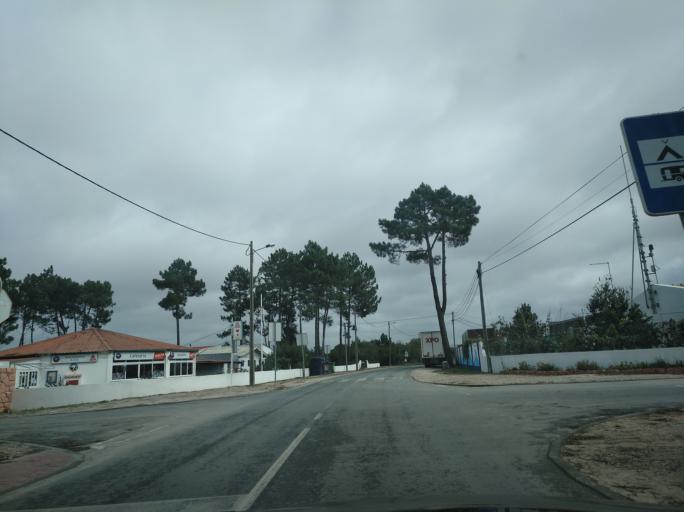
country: PT
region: Setubal
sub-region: Santiago do Cacem
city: Santo Andre
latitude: 38.1310
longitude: -8.7815
